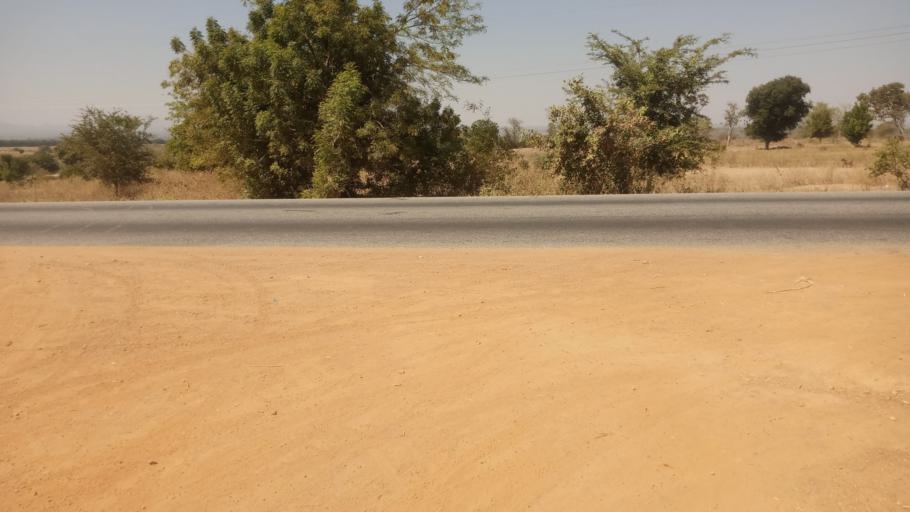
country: NG
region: Adamawa
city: Mayo Belwa
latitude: 9.1660
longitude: 12.0982
